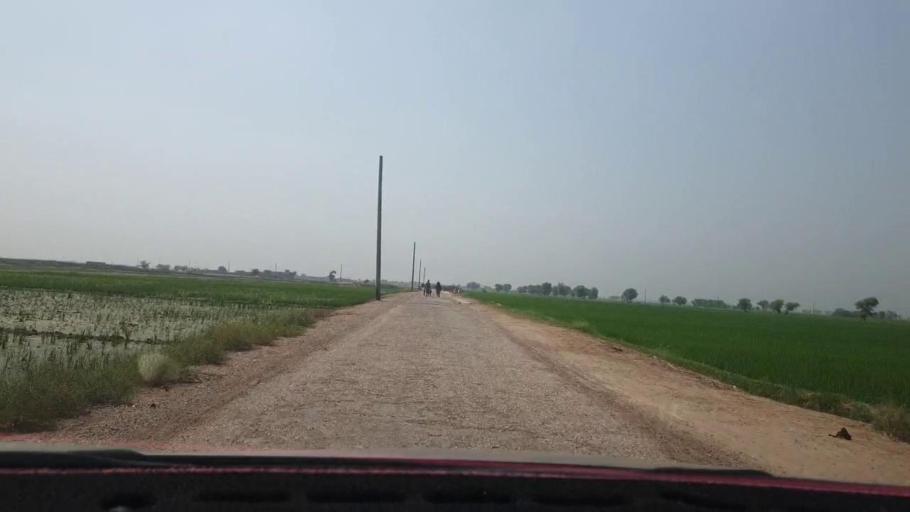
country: PK
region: Sindh
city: Warah
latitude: 27.4097
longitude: 67.8447
